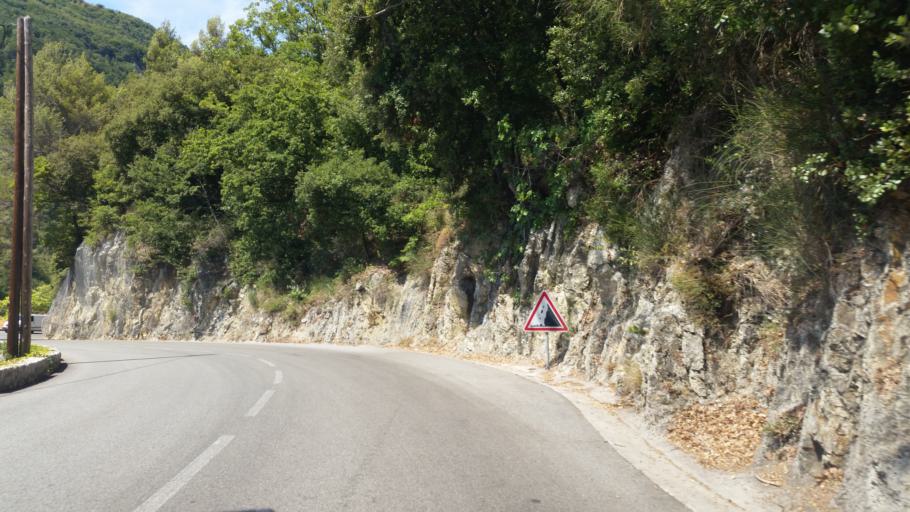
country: FR
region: Provence-Alpes-Cote d'Azur
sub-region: Departement des Alpes-Maritimes
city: Sainte-Agnes
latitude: 43.8292
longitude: 7.4793
